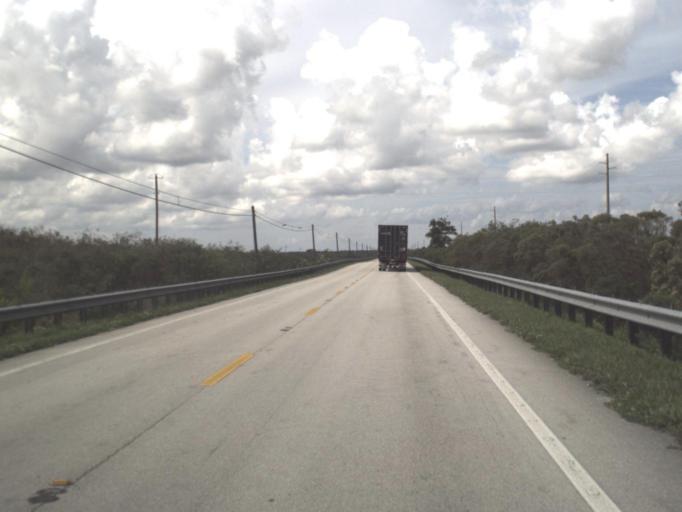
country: US
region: Florida
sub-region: Highlands County
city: Lake Placid
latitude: 27.2088
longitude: -81.2292
